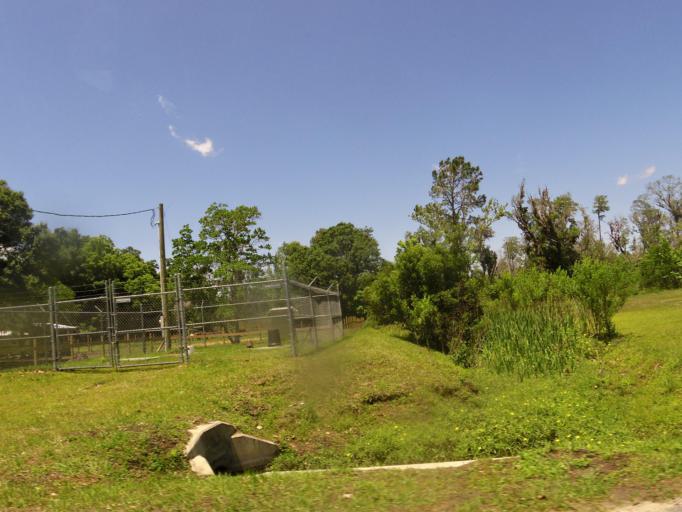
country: US
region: Florida
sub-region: Bradford County
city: Starke
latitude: 30.0468
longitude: -82.0758
